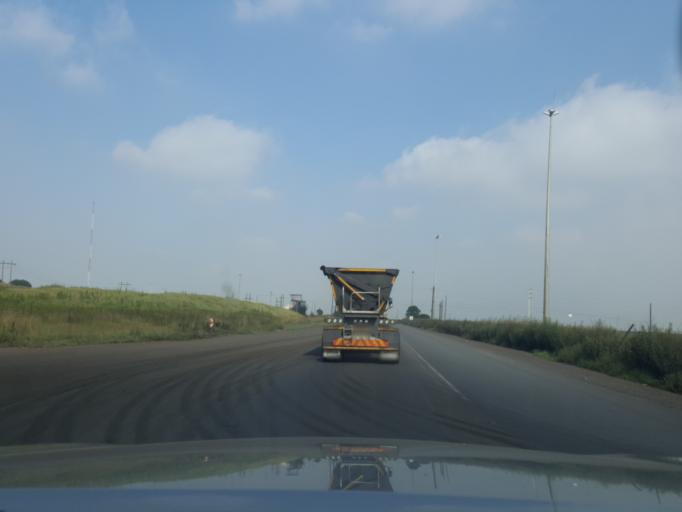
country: ZA
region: Mpumalanga
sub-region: Nkangala District Municipality
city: Witbank
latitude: -26.0143
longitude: 29.3532
